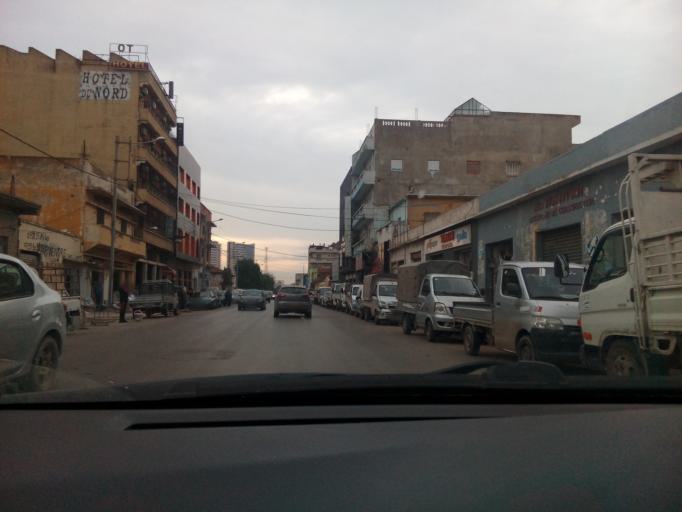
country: DZ
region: Oran
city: Oran
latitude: 35.6865
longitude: -0.6411
